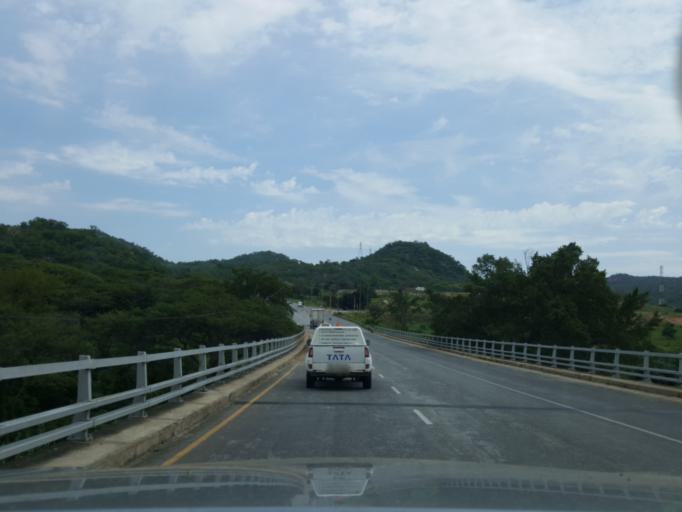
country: ZA
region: Mpumalanga
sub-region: Ehlanzeni District
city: Nelspruit
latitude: -25.4699
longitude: 31.0933
